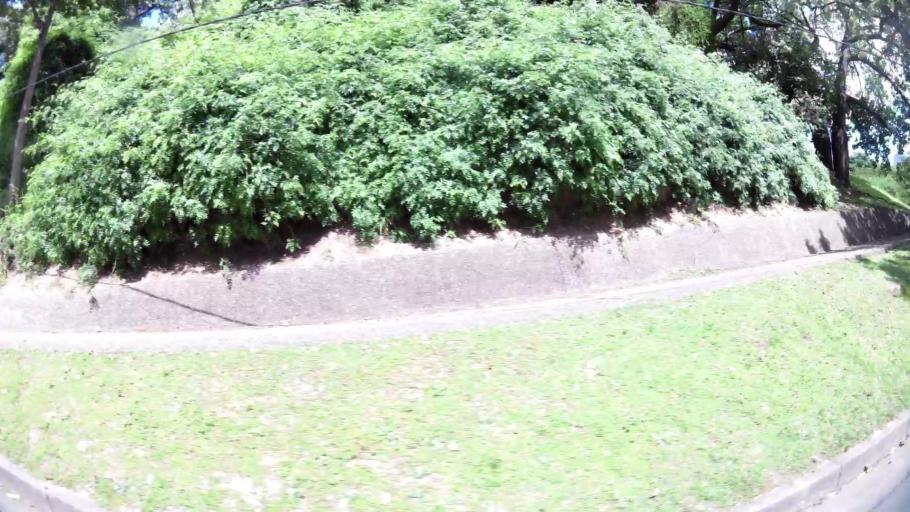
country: AR
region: Santa Fe
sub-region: Departamento de Rosario
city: Rosario
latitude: -32.9585
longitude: -60.6219
